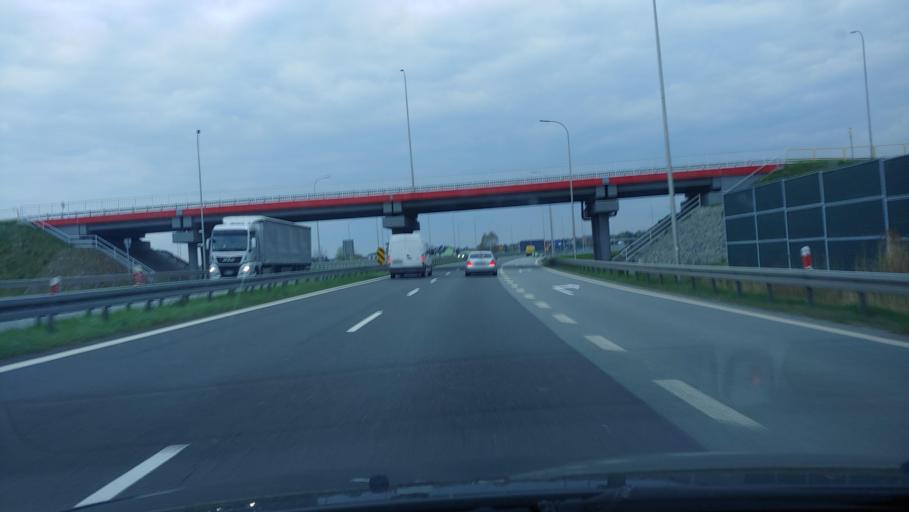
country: PL
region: Silesian Voivodeship
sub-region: Powiat bierunsko-ledzinski
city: Ledziny
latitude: 50.1431
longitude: 19.0998
